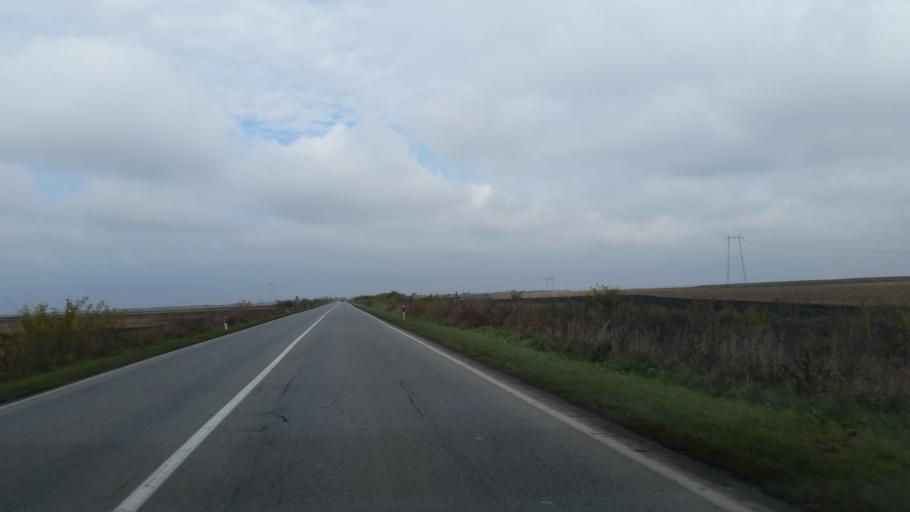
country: RS
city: Melenci
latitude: 45.4844
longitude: 20.3335
